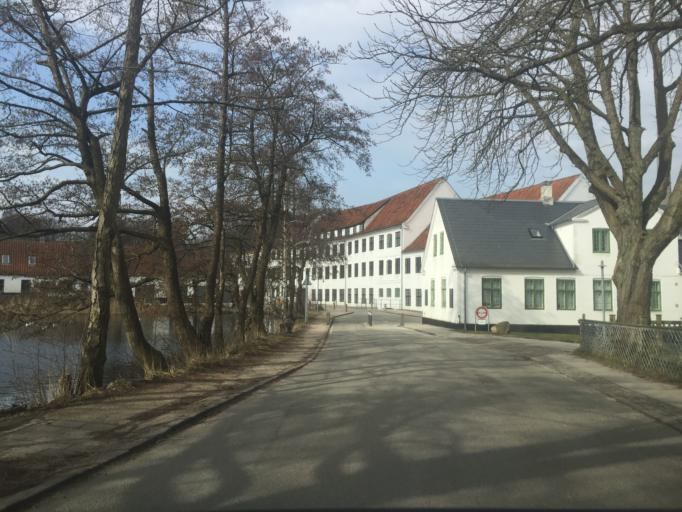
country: DK
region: Capital Region
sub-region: Lyngby-Tarbaek Kommune
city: Kongens Lyngby
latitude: 55.7939
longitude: 12.5006
